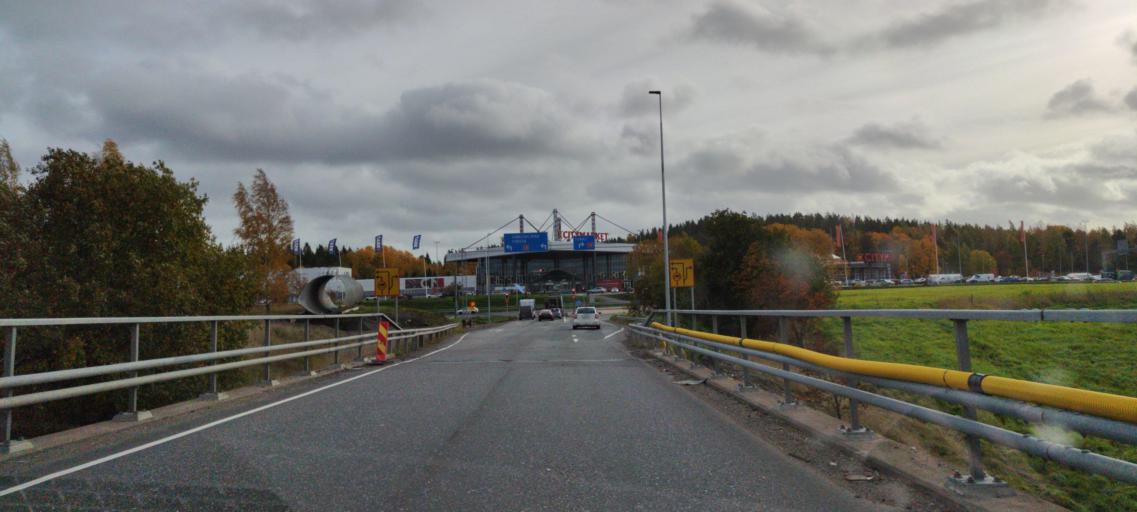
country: FI
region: Varsinais-Suomi
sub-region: Turku
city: Kaarina
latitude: 60.4718
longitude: 22.3567
